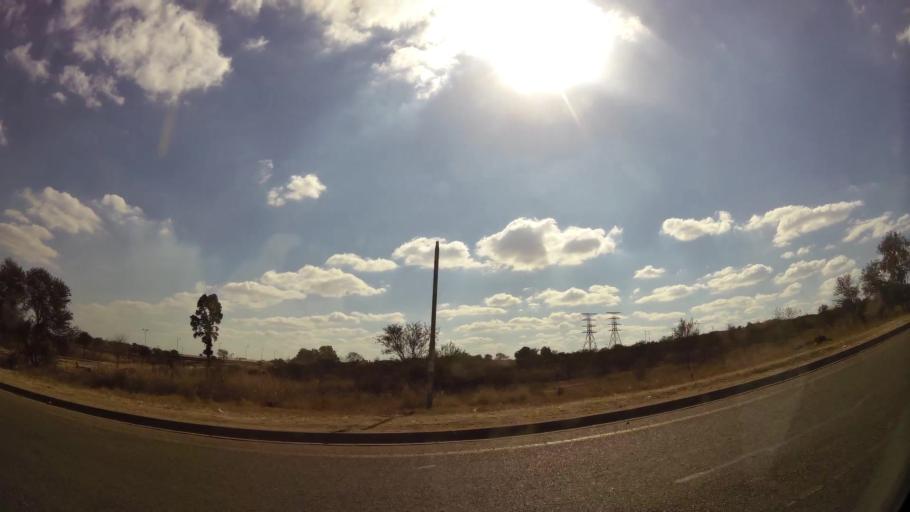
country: ZA
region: Gauteng
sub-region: City of Tshwane Metropolitan Municipality
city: Cullinan
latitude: -25.7418
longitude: 28.3771
